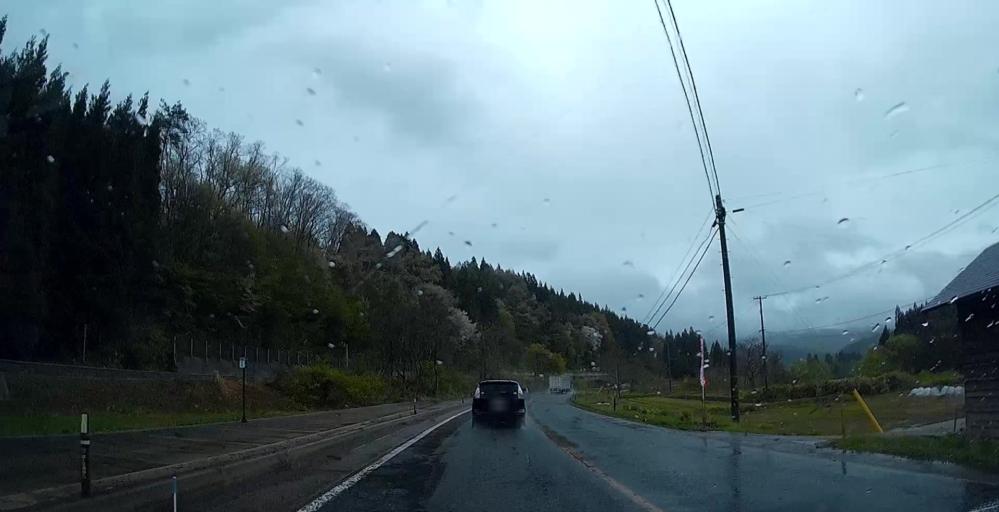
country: JP
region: Yamagata
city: Nagai
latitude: 38.0448
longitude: 139.7688
